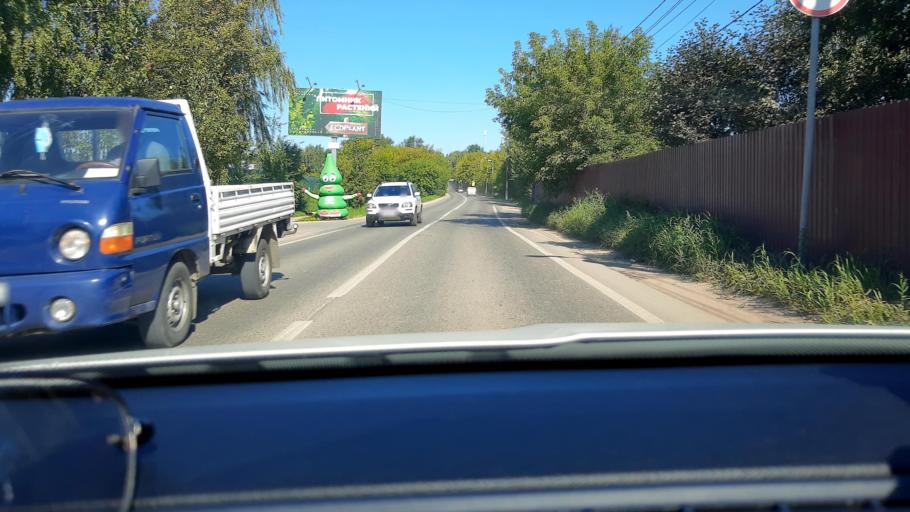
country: RU
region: Moskovskaya
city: Barvikha
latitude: 55.7621
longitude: 37.2288
